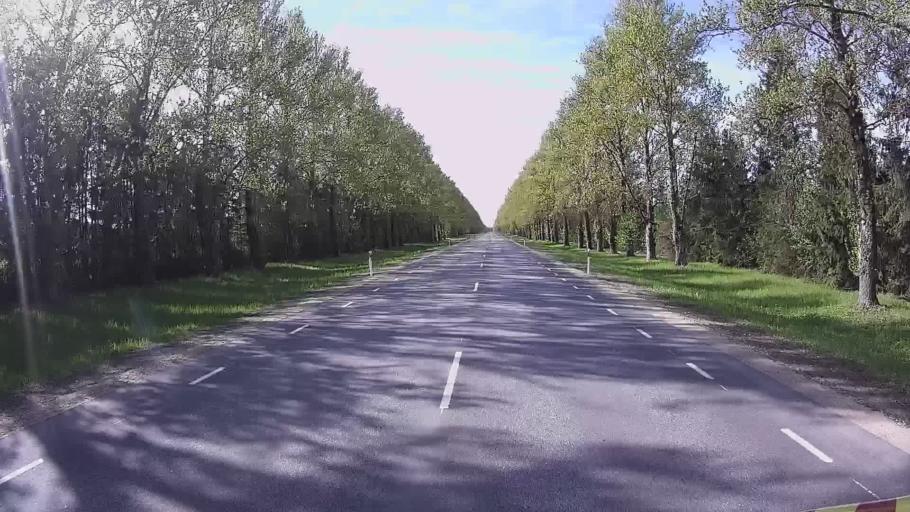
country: EE
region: Polvamaa
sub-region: Polva linn
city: Polva
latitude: 58.2921
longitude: 27.0016
